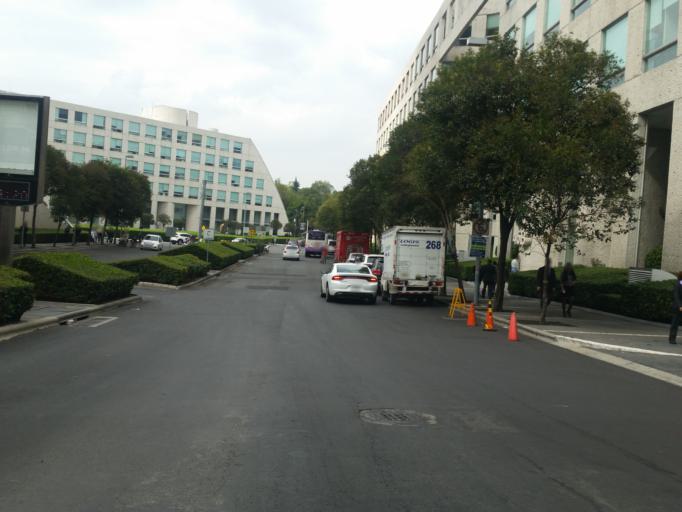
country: MX
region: Mexico City
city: Col. Bosques de las Lomas
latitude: 19.3880
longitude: -99.2501
